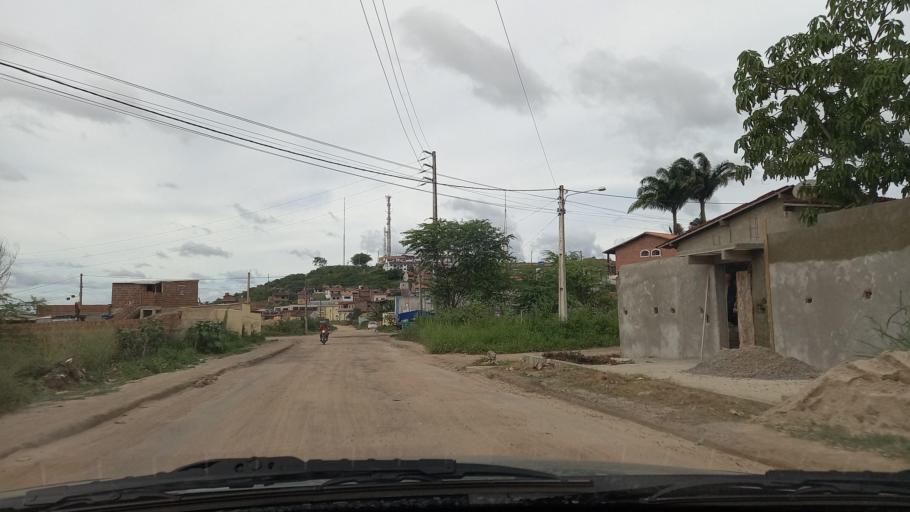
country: BR
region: Pernambuco
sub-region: Gravata
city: Gravata
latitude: -8.2134
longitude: -35.5790
